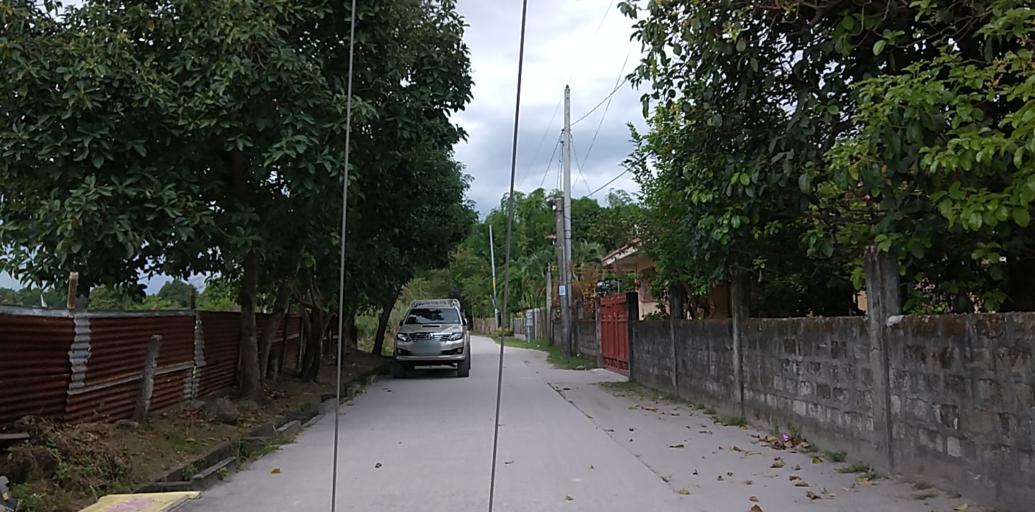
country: PH
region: Central Luzon
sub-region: Province of Pampanga
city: Pulung Santol
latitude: 15.0409
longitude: 120.5659
